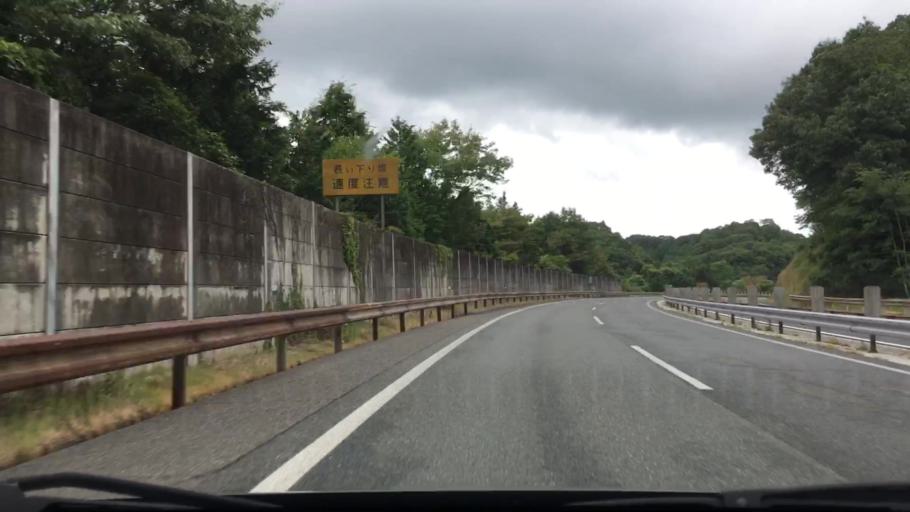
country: JP
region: Okayama
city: Niimi
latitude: 34.9025
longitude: 133.3012
